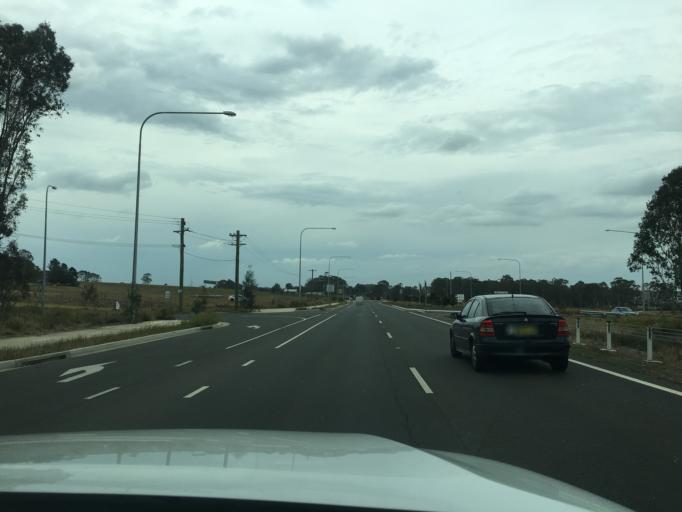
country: AU
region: New South Wales
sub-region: Campbelltown Municipality
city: Denham Court
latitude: -33.9851
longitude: 150.7954
